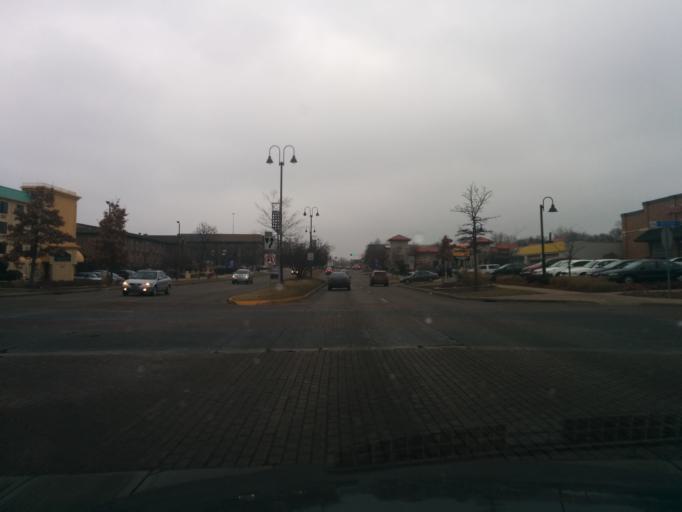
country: US
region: Wisconsin
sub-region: Milwaukee County
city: Whitefish Bay
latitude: 43.1149
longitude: -87.9167
